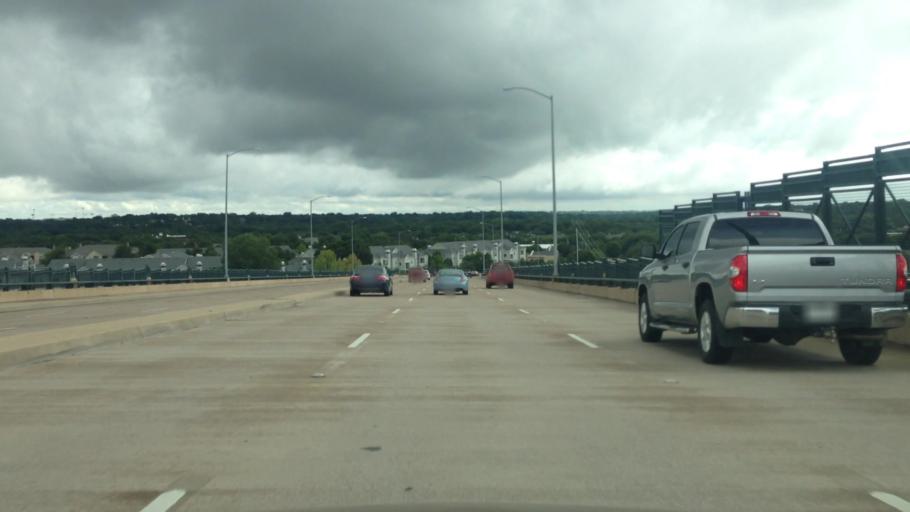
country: US
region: Texas
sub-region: Tarrant County
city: Westworth
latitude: 32.7177
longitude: -97.3857
